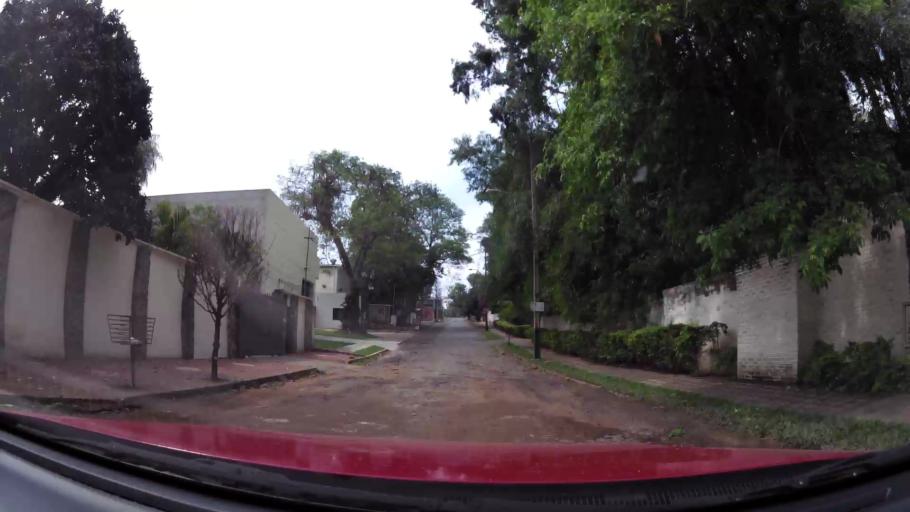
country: PY
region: Asuncion
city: Asuncion
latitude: -25.2917
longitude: -57.5829
